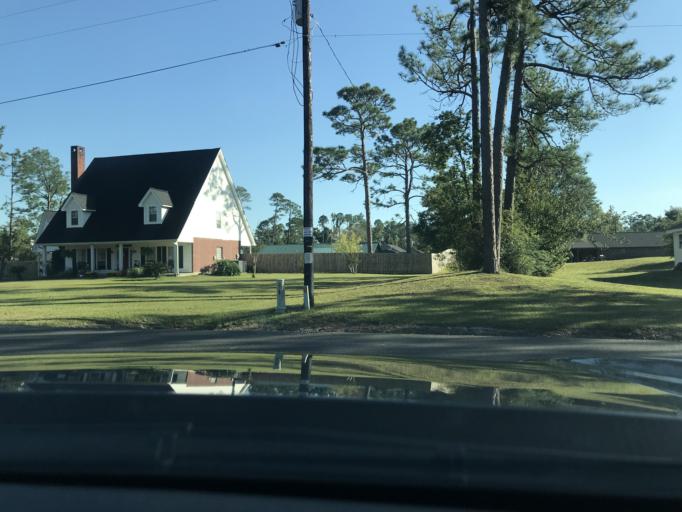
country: US
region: Louisiana
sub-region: Calcasieu Parish
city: Westlake
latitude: 30.3184
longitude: -93.2732
